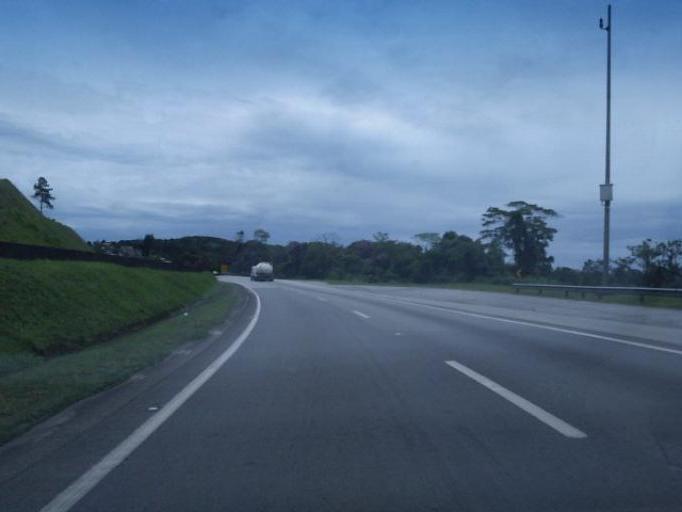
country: BR
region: Sao Paulo
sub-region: Juquitiba
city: Juquitiba
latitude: -23.9761
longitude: -47.1435
